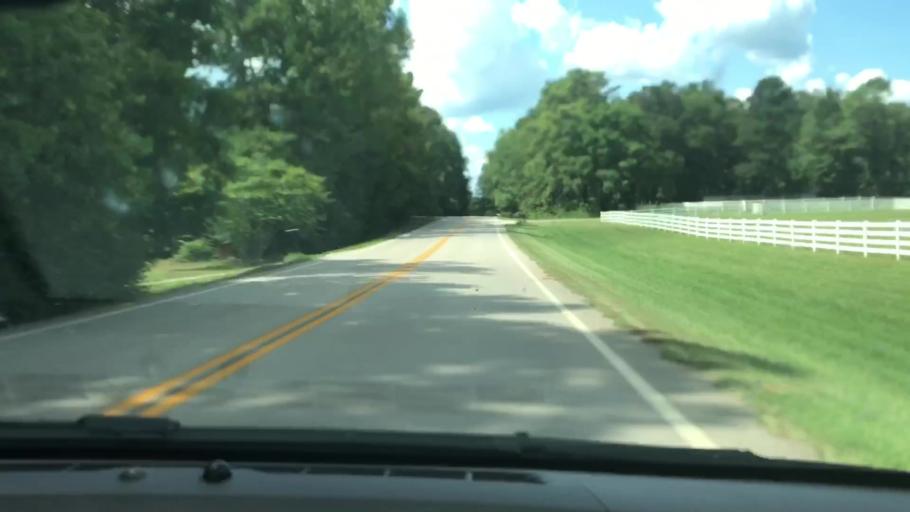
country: US
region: Georgia
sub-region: Troup County
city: La Grange
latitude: 33.1120
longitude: -85.0822
